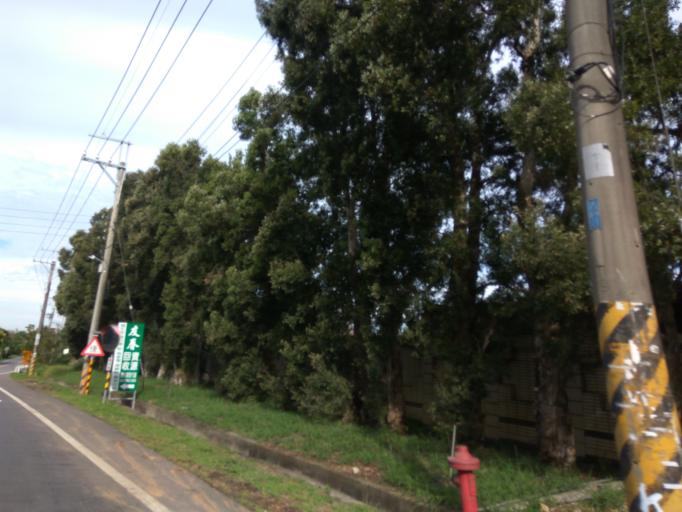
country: TW
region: Taiwan
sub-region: Hsinchu
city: Zhubei
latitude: 24.9568
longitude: 121.1210
